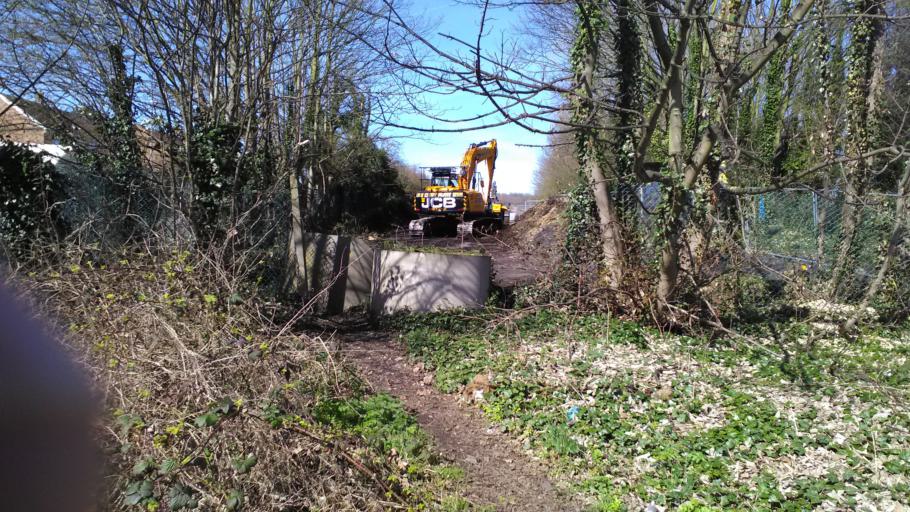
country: GB
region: England
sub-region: Nottinghamshire
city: Arnold
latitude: 52.9806
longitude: -1.0864
